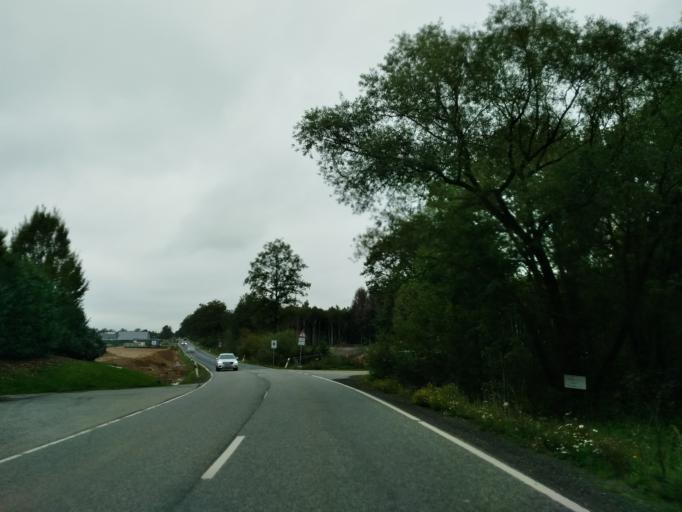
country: DE
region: Rheinland-Pfalz
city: Windhagen
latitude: 50.6440
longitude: 7.3453
